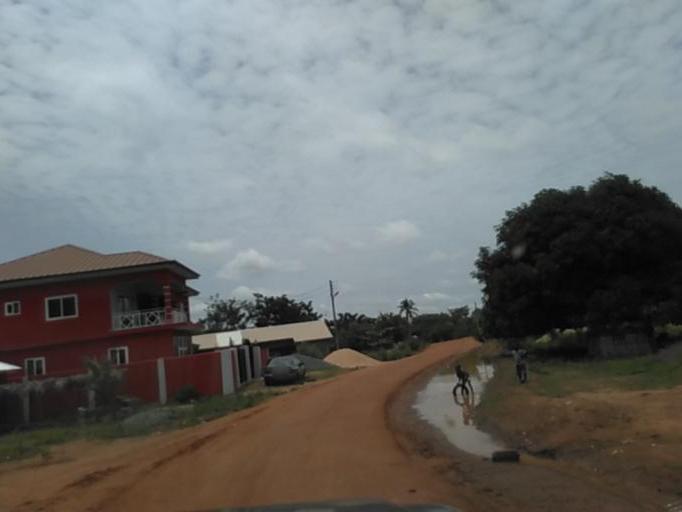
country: GH
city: Akropong
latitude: 6.0297
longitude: 0.3719
